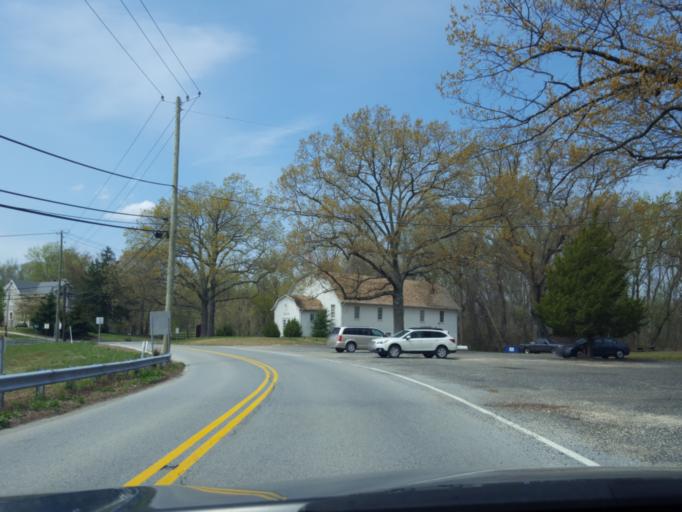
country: US
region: Maryland
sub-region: Prince George's County
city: Croom
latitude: 38.7481
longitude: -76.7589
